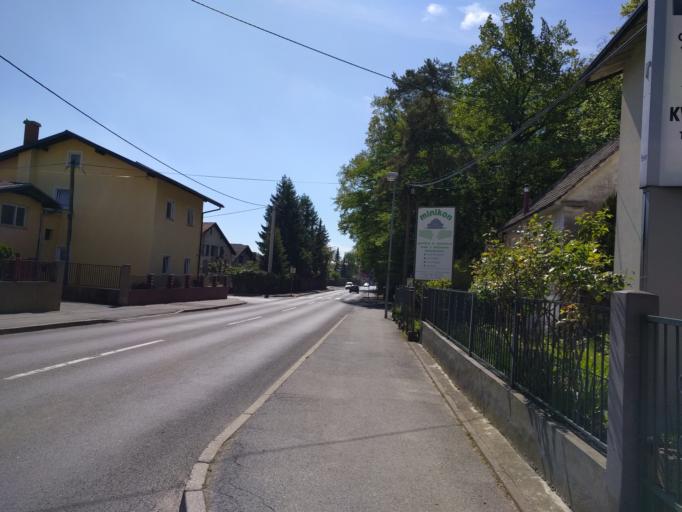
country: SI
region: Maribor
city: Maribor
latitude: 46.5420
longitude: 15.6822
